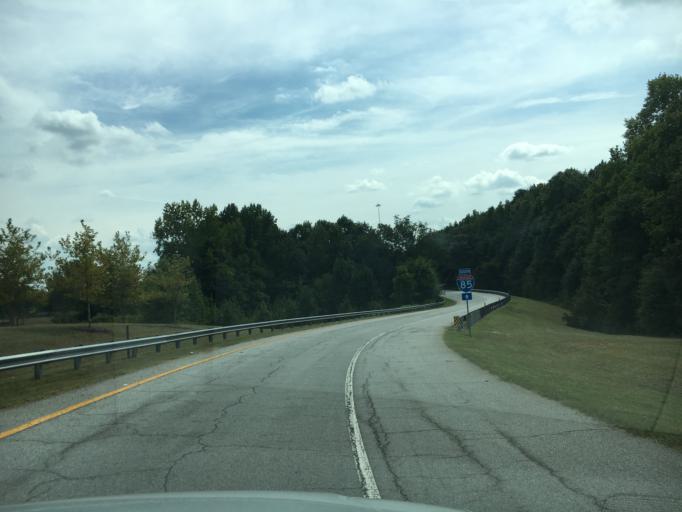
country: US
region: South Carolina
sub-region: Anderson County
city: Northlake
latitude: 34.5759
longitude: -82.7133
